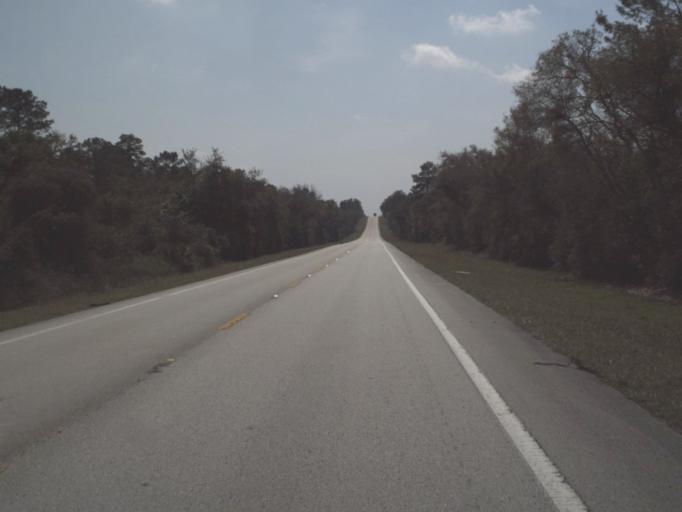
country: US
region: Florida
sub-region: Lake County
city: Astor
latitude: 29.1833
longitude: -81.6524
